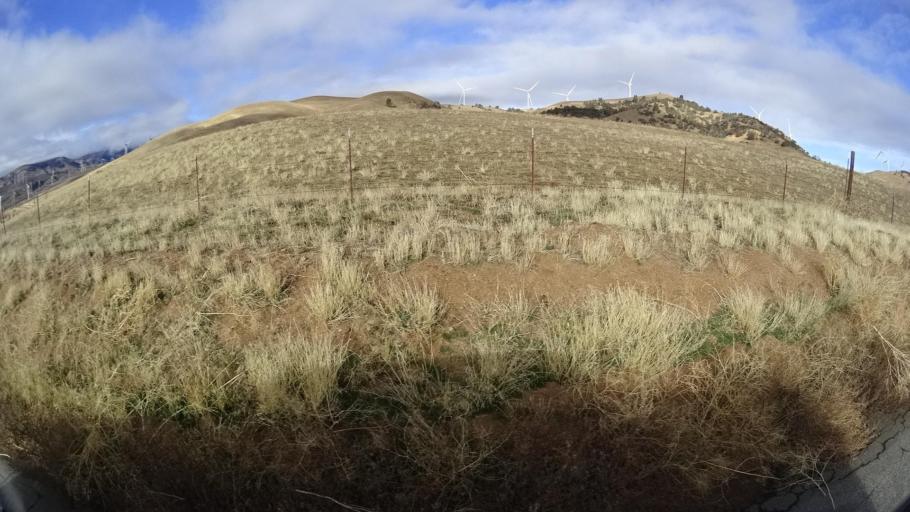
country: US
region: California
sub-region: Kern County
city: Tehachapi
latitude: 35.0705
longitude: -118.3424
